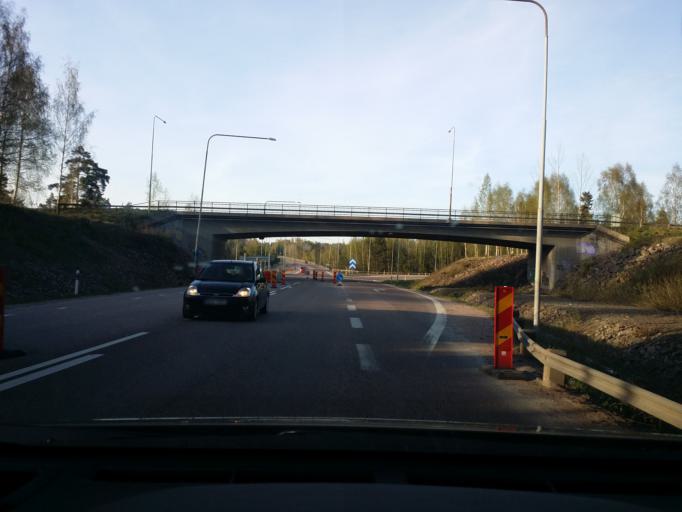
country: SE
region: Dalarna
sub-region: Avesta Kommun
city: Avesta
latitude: 60.1435
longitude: 16.1949
